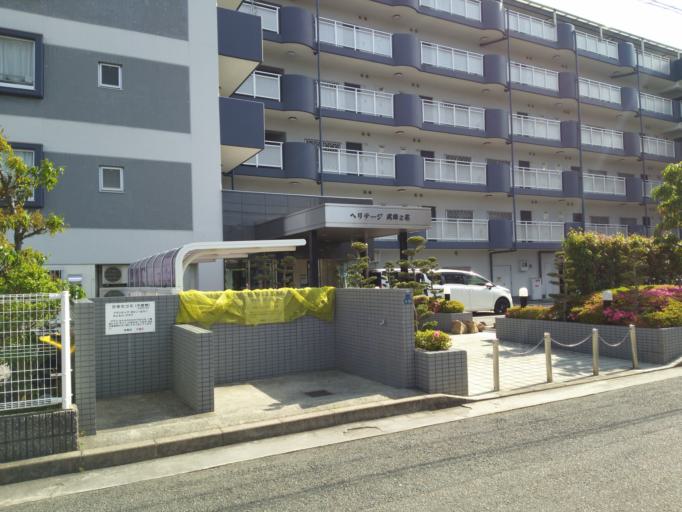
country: JP
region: Hyogo
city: Amagasaki
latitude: 34.7441
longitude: 135.3964
